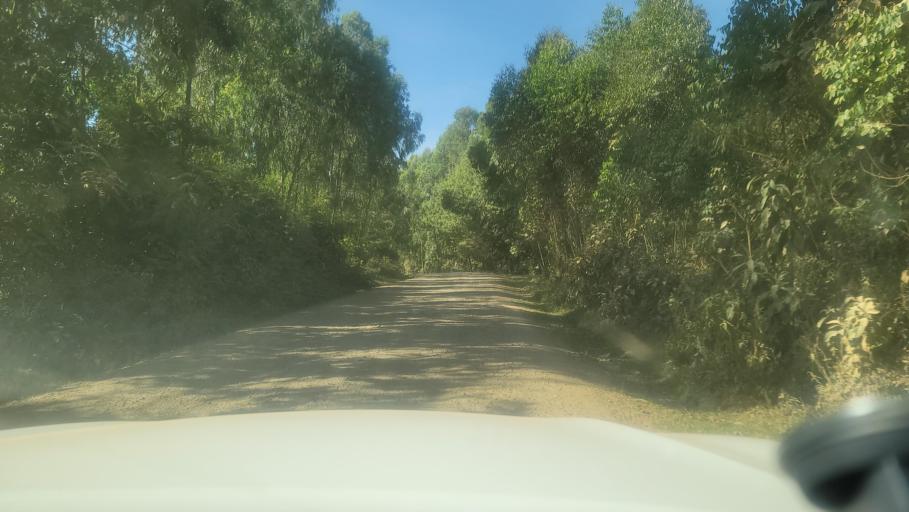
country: ET
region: Oromiya
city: Agaro
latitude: 7.8051
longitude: 36.5009
